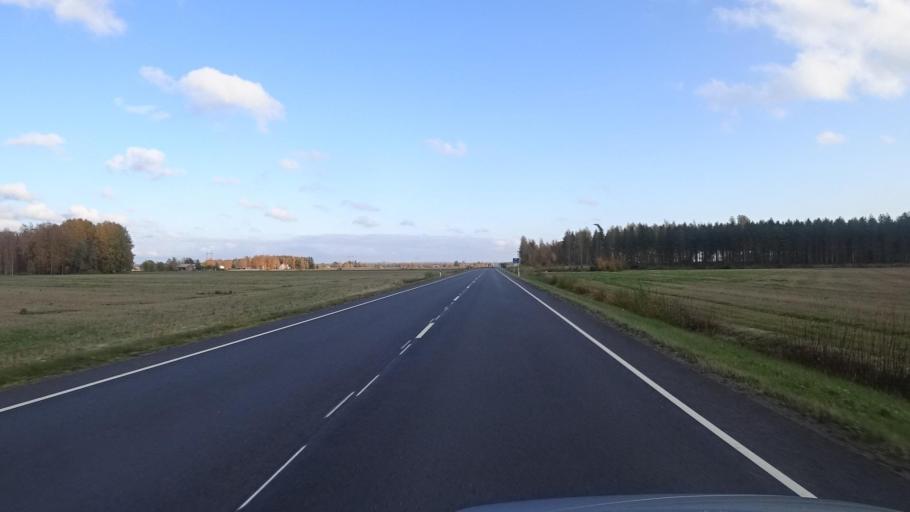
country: FI
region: Satakunta
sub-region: Rauma
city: Koeylioe
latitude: 61.0721
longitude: 22.3065
